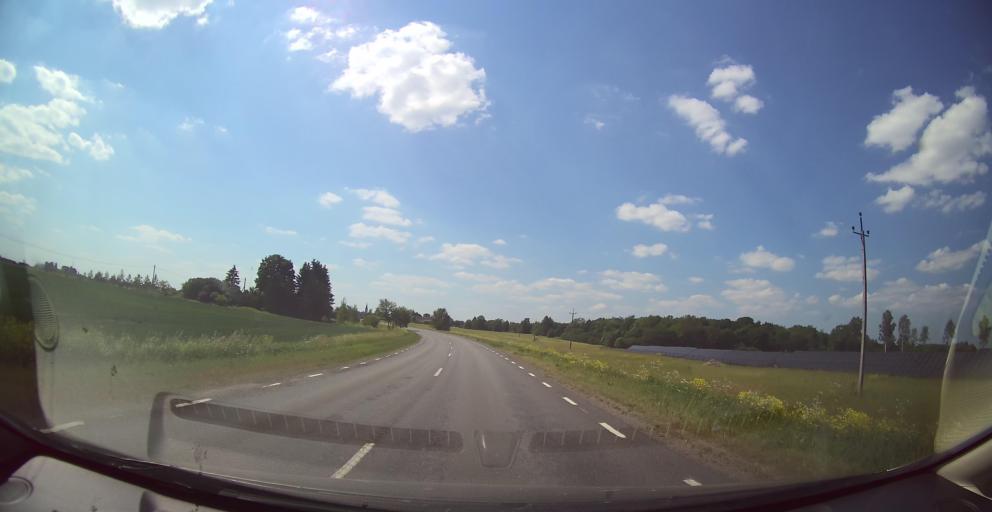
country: EE
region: Harju
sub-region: Raasiku vald
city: Raasiku
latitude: 59.3776
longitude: 25.2101
